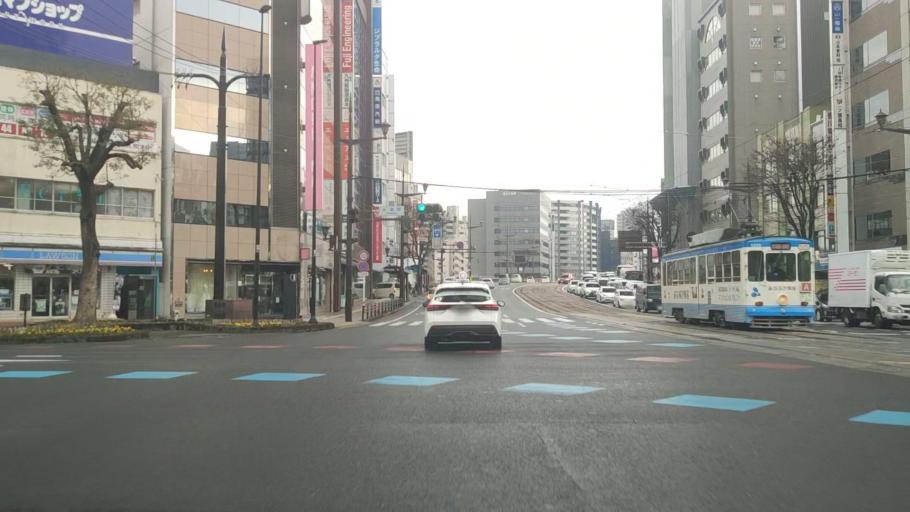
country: JP
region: Kumamoto
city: Kumamoto
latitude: 32.8023
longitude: 130.7129
